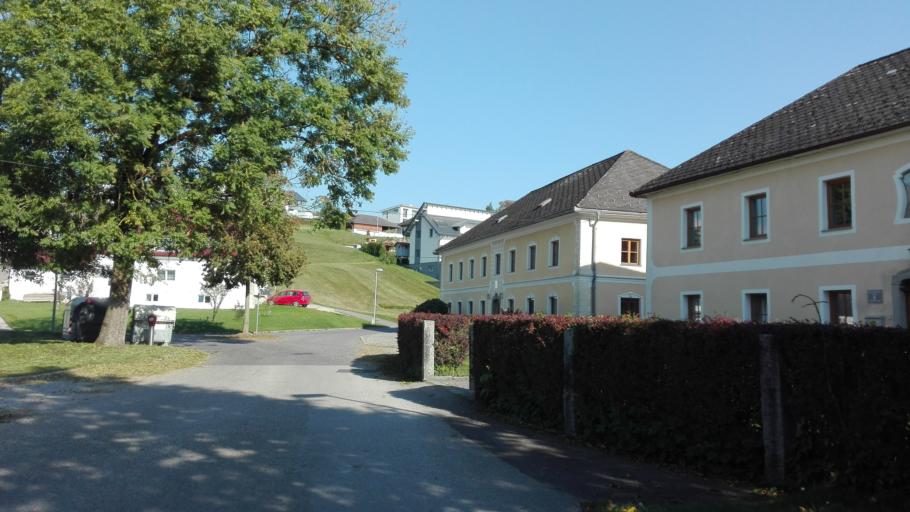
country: AT
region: Upper Austria
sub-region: Politischer Bezirk Perg
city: Perg
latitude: 48.2579
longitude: 14.5917
